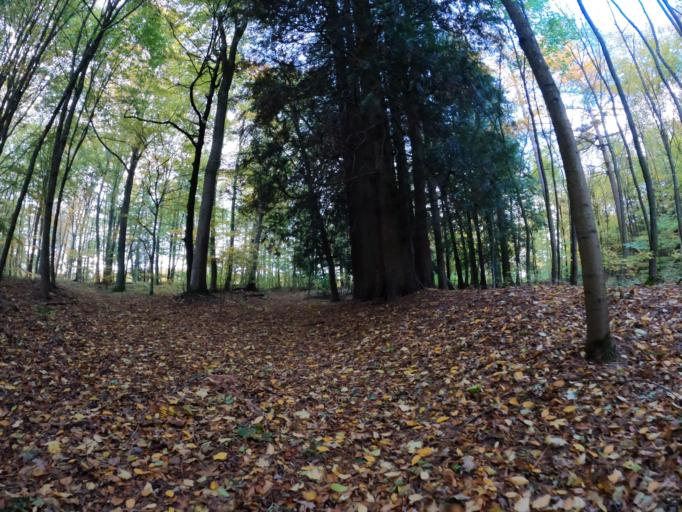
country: PL
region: West Pomeranian Voivodeship
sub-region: Powiat mysliborski
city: Barlinek
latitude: 52.9667
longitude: 15.2570
